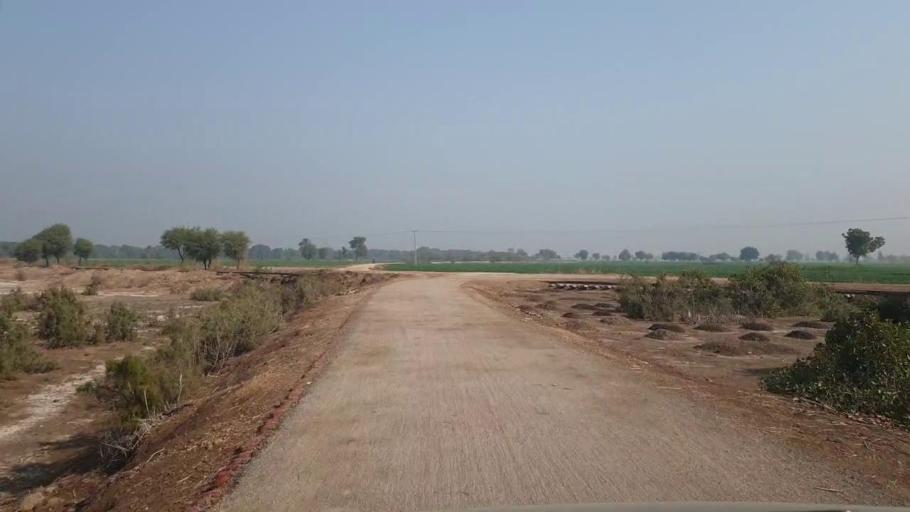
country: PK
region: Sindh
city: Sakrand
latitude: 26.0051
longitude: 68.3562
